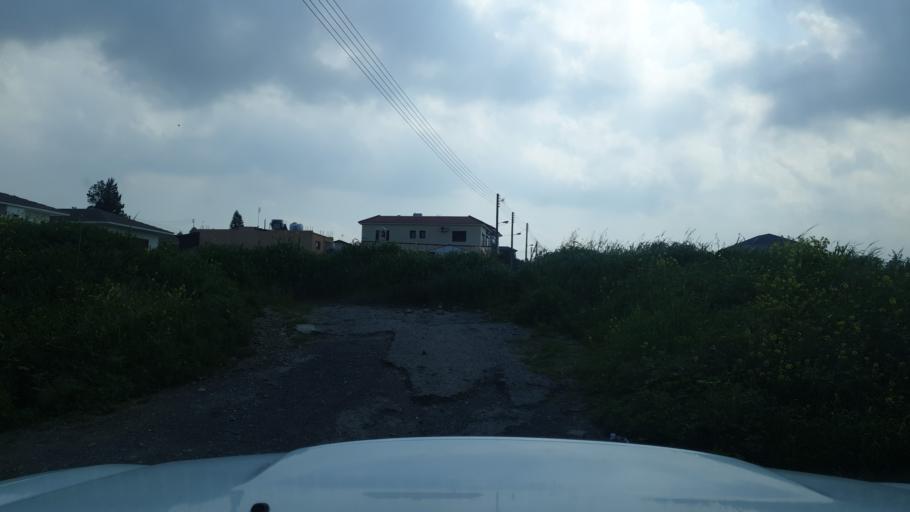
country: CY
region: Lefkosia
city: Kato Deftera
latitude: 35.0898
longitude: 33.2816
